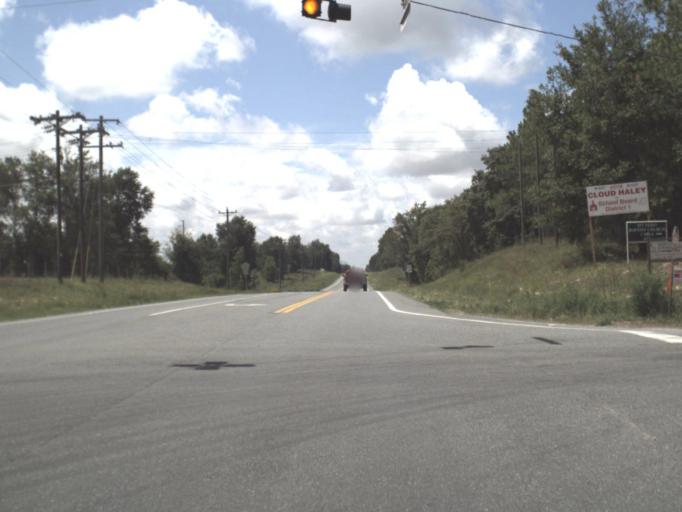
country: US
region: Florida
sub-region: Gilchrist County
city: Trenton
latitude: 29.7962
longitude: -82.8669
